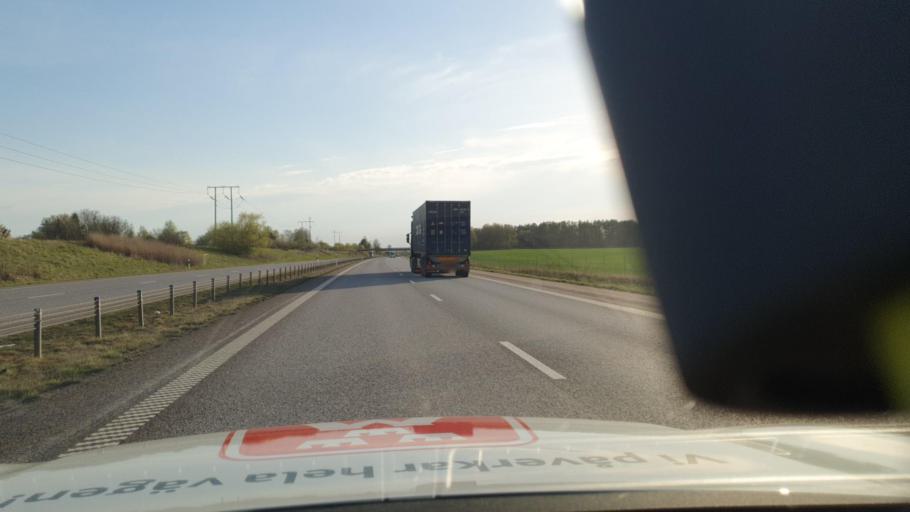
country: SE
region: OEstergoetland
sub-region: Linkopings Kommun
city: Ekangen
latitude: 58.4365
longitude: 15.6934
